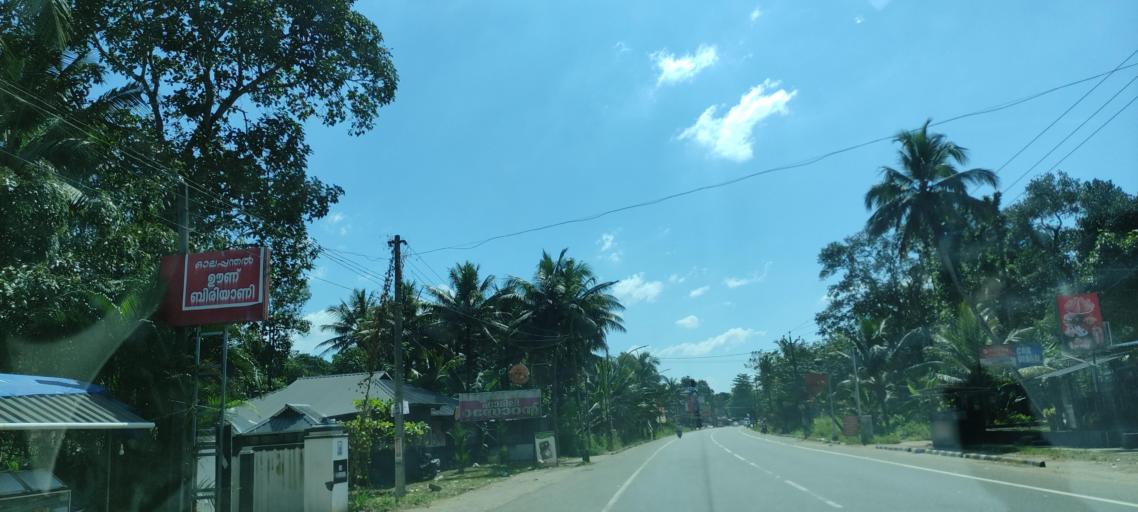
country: IN
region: Kerala
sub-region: Pattanamtitta
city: Adur
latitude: 9.1509
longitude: 76.7287
